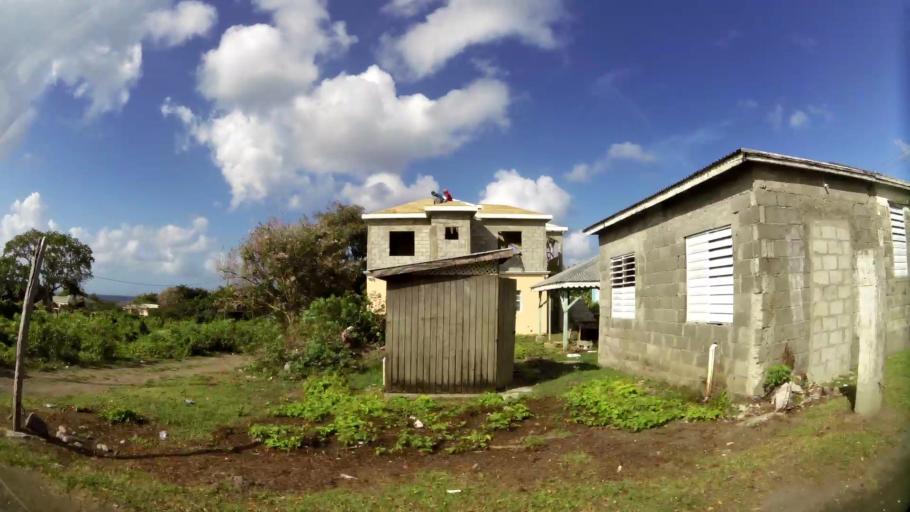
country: KN
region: Saint Paul Charlestown
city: Charlestown
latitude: 17.1292
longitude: -62.6267
